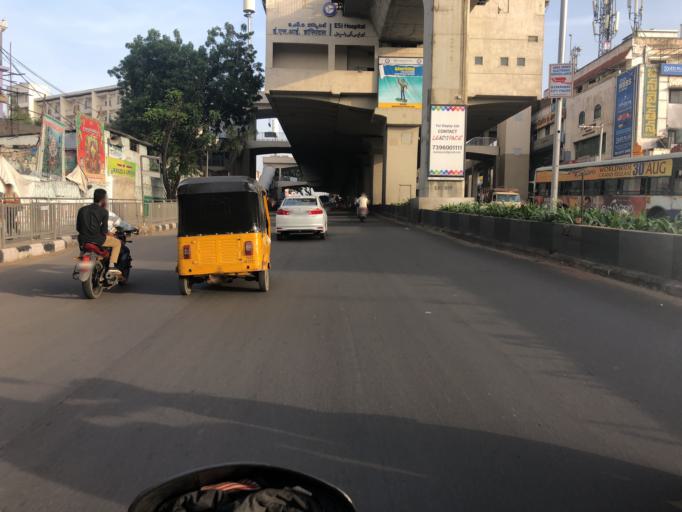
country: IN
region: Telangana
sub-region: Rangareddi
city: Kukatpalli
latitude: 17.4483
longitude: 78.4379
